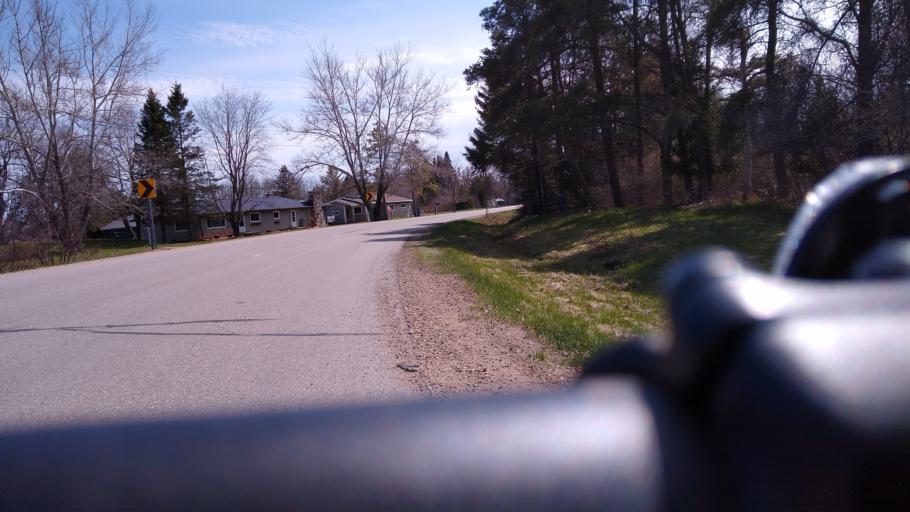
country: US
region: Michigan
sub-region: Delta County
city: Escanaba
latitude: 45.6801
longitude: -87.1442
